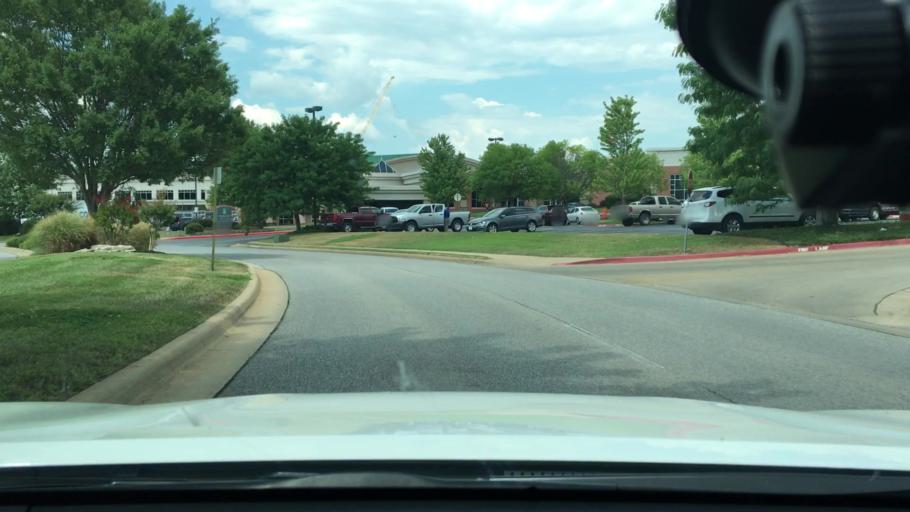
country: US
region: Arkansas
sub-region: Benton County
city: Cave Springs
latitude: 36.3054
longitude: -94.1870
